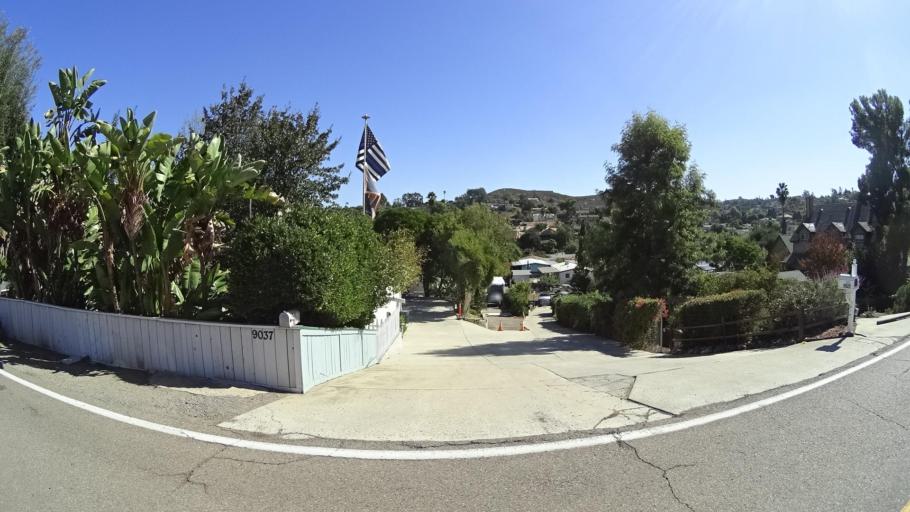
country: US
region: California
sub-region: San Diego County
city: Winter Gardens
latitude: 32.8409
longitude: -116.9355
